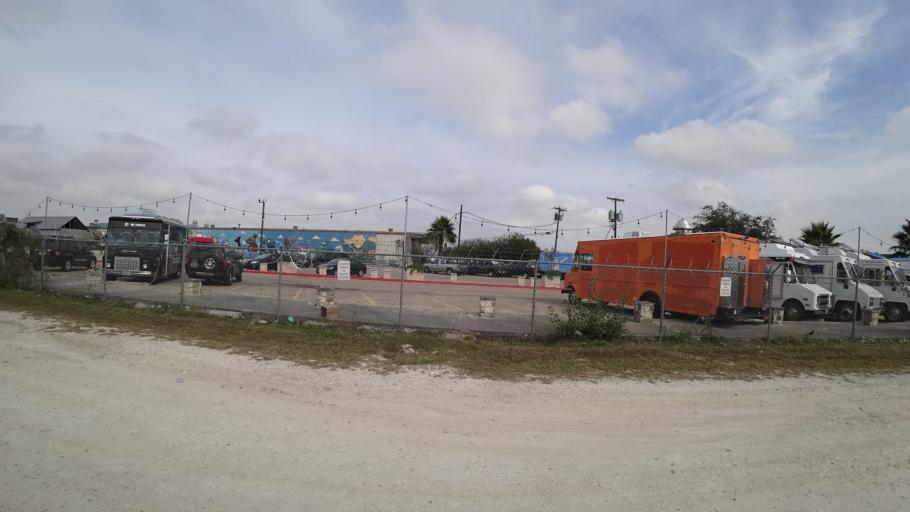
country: US
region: Texas
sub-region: Travis County
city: Windemere
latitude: 30.4498
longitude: -97.6623
